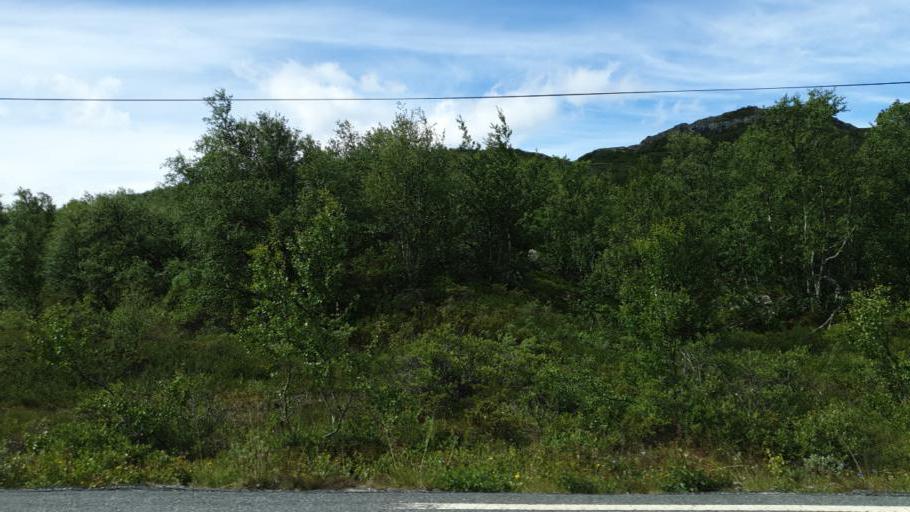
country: NO
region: Oppland
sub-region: Oystre Slidre
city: Heggenes
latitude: 61.4992
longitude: 8.8434
